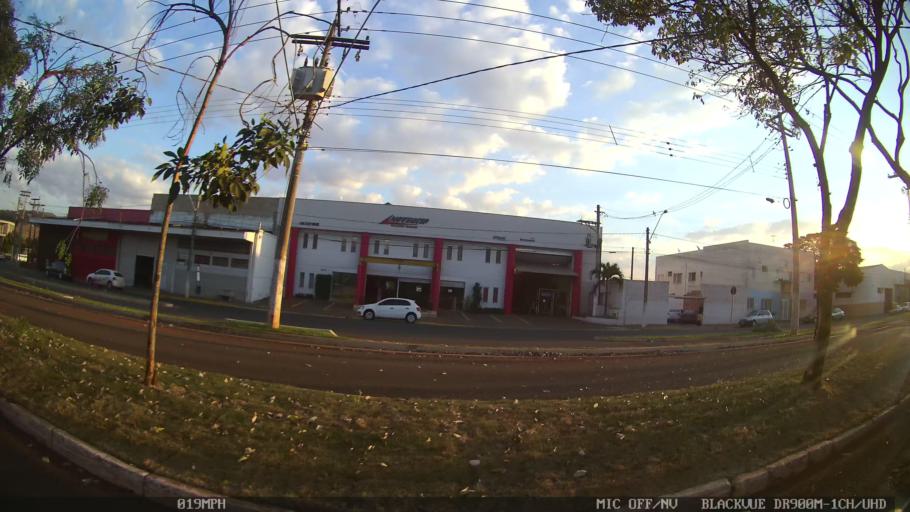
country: BR
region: Sao Paulo
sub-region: Ribeirao Preto
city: Ribeirao Preto
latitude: -21.1518
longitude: -47.7814
